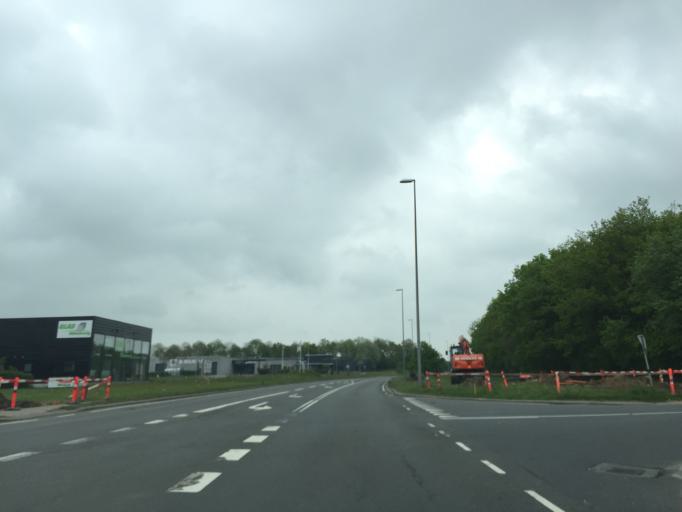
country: DK
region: Central Jutland
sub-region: Silkeborg Kommune
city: Silkeborg
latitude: 56.2012
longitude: 9.5766
